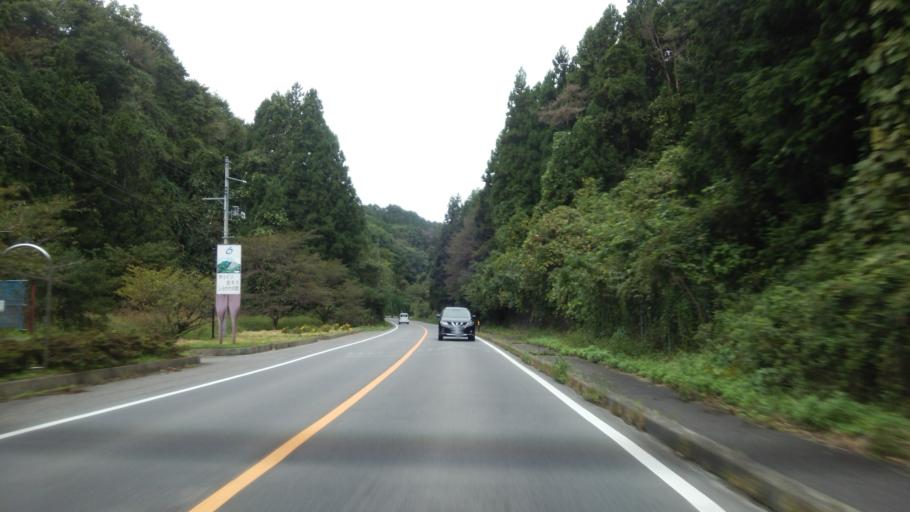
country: JP
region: Fukushima
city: Sukagawa
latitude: 37.1723
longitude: 140.2185
